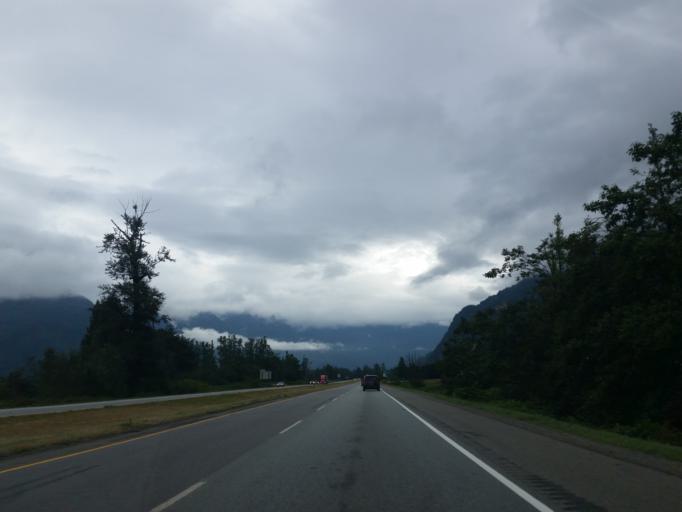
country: CA
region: British Columbia
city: Agassiz
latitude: 49.3189
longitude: -121.6264
